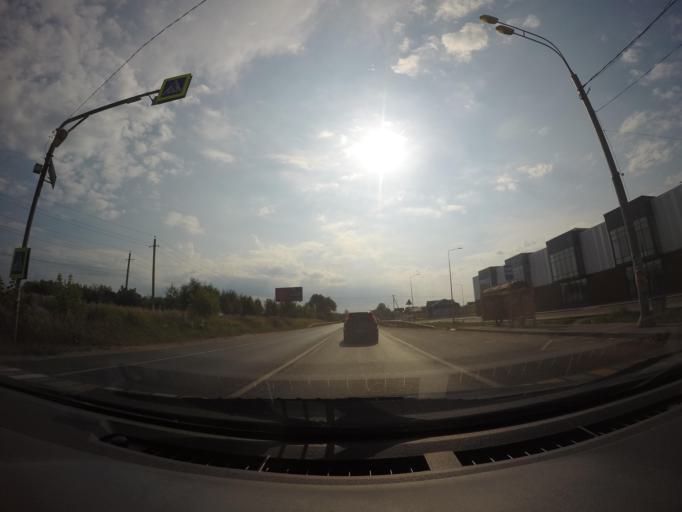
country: RU
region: Moskovskaya
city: Rechitsy
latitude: 55.6038
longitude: 38.4340
